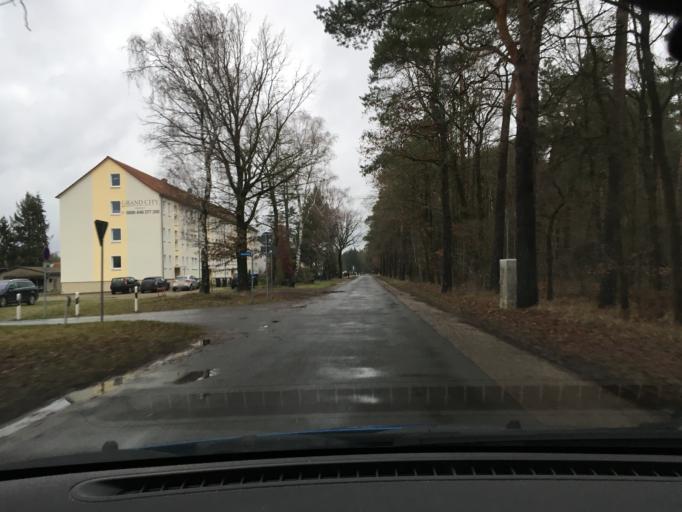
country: DE
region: Mecklenburg-Vorpommern
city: Nostorf
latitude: 53.4332
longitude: 10.6939
